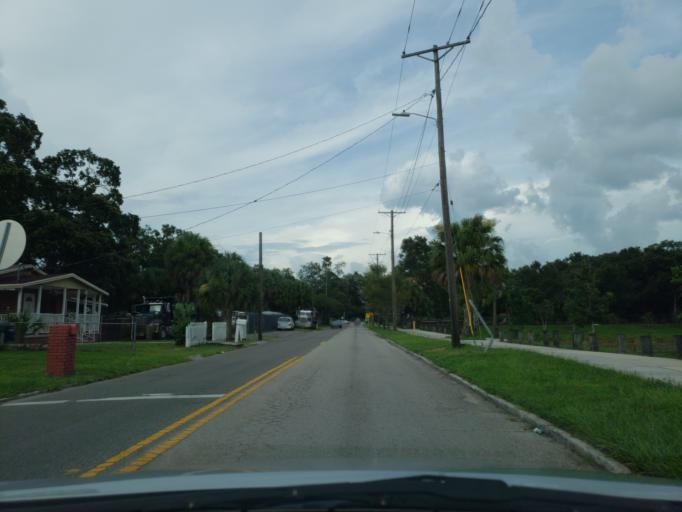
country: US
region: Florida
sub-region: Hillsborough County
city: East Lake-Orient Park
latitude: 27.9888
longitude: -82.4285
